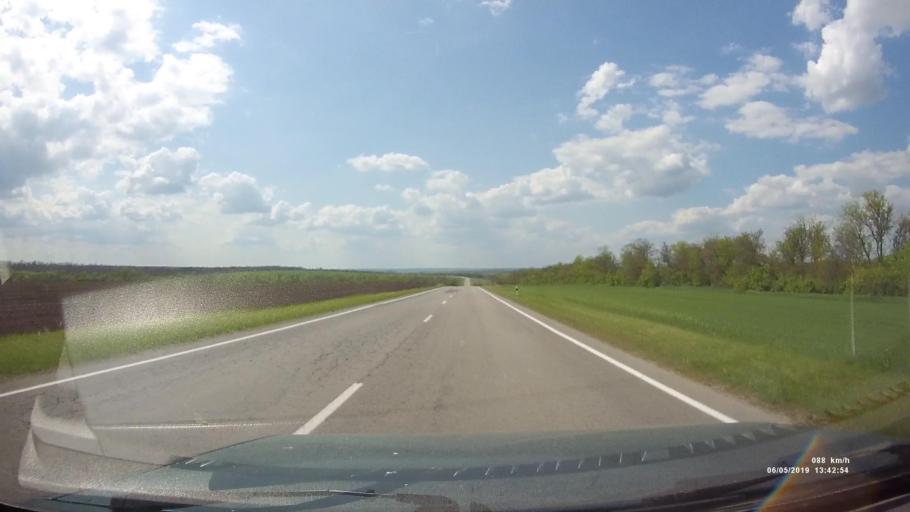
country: RU
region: Rostov
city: Semikarakorsk
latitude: 47.6598
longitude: 40.6486
